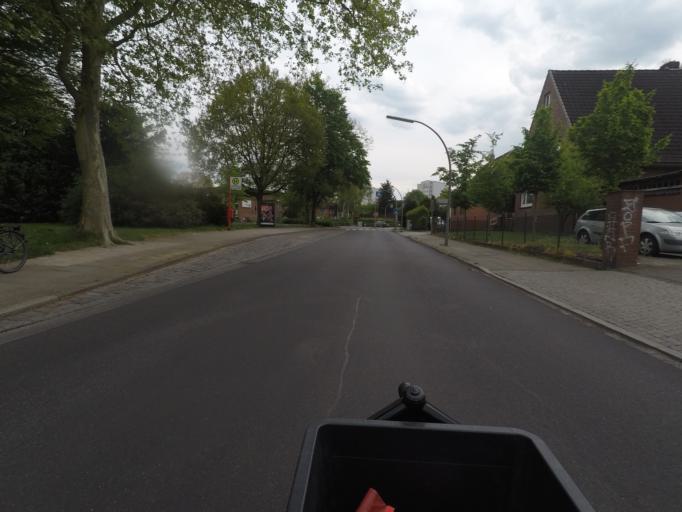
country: DE
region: Hamburg
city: Steilshoop
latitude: 53.6068
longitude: 10.0809
